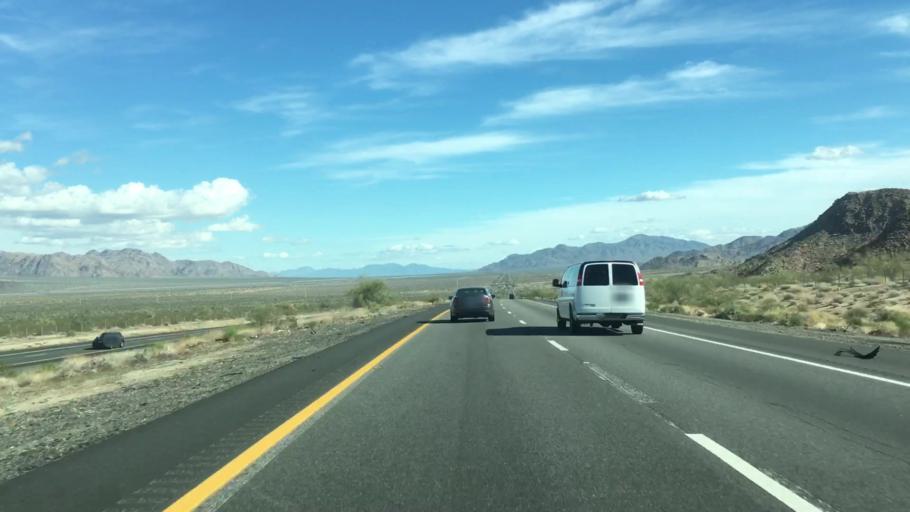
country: US
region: California
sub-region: Riverside County
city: Mecca
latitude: 33.6659
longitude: -115.6839
